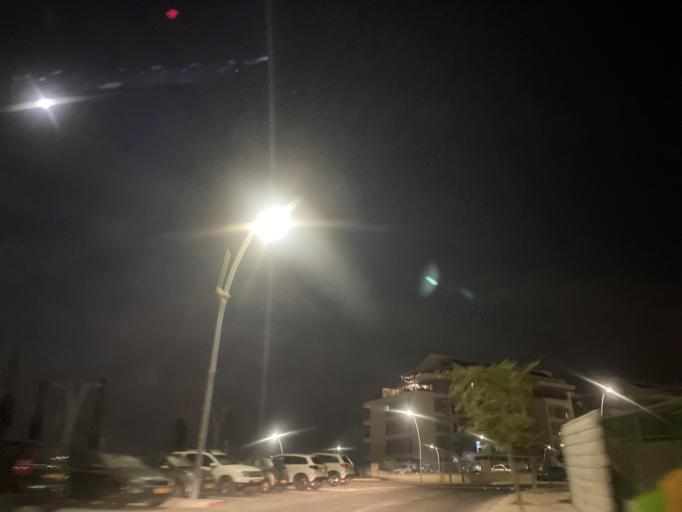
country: IL
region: Haifa
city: Daliyat el Karmil
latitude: 32.6376
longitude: 35.0777
